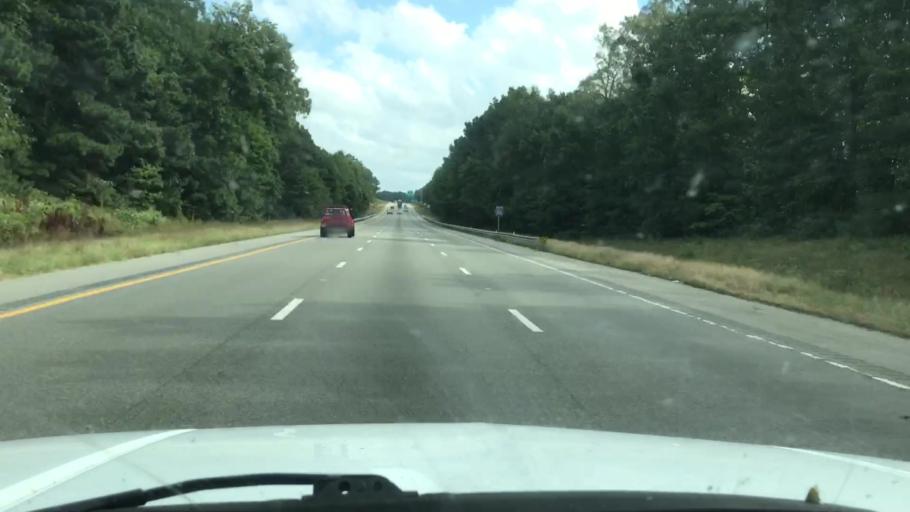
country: US
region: Virginia
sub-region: Henrico County
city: Short Pump
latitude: 37.6736
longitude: -77.5706
